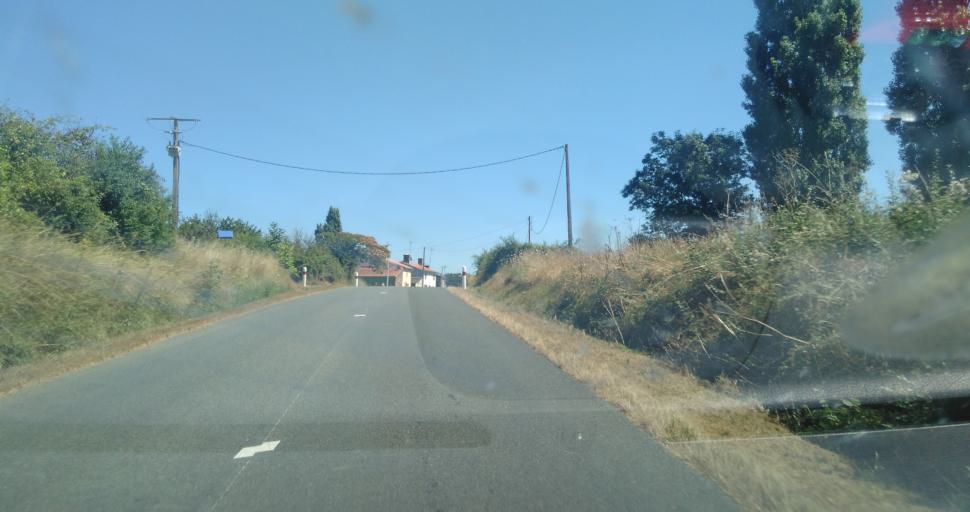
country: FR
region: Pays de la Loire
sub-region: Departement de la Vendee
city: Sainte-Hermine
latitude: 46.5772
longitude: -1.0424
